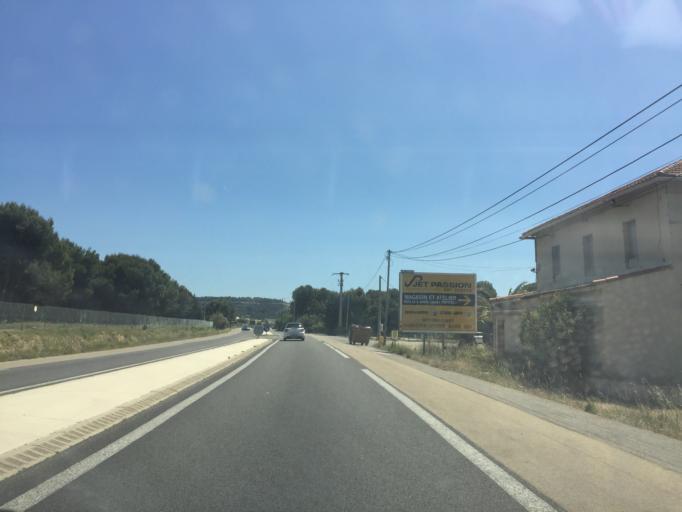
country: FR
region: Provence-Alpes-Cote d'Azur
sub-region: Departement des Bouches-du-Rhone
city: Rognac
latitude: 43.4820
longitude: 5.2248
